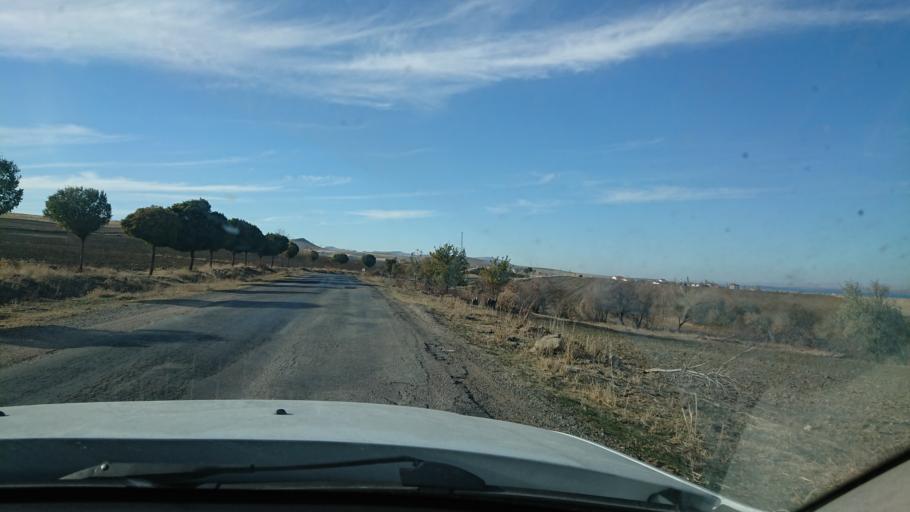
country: TR
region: Aksaray
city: Sariyahsi
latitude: 38.9727
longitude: 33.8611
